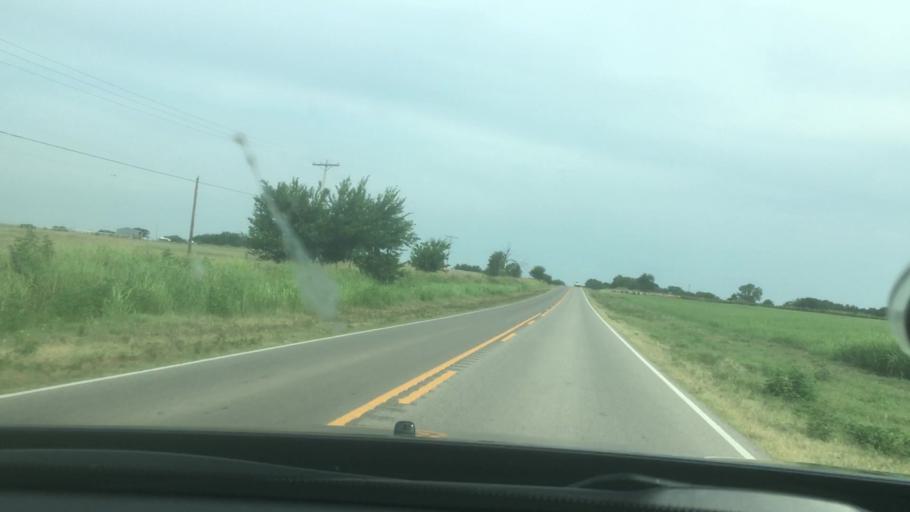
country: US
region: Oklahoma
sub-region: Garvin County
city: Maysville
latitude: 34.8057
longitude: -97.3701
